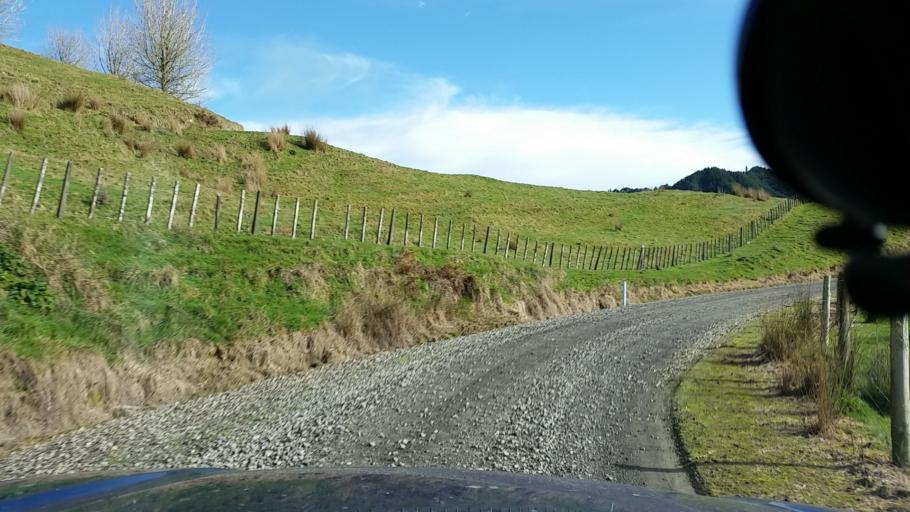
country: NZ
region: Taranaki
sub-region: New Plymouth District
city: Waitara
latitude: -39.0339
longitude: 174.7735
